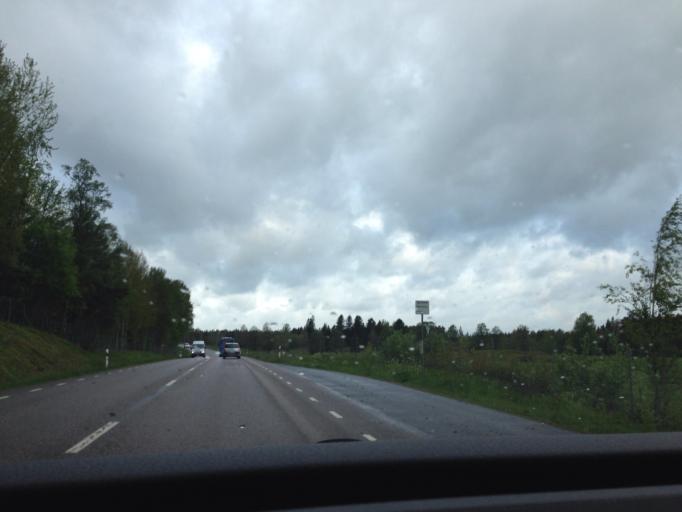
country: SE
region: Vaestra Goetaland
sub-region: Tibro Kommun
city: Tibro
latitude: 58.4174
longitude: 14.1102
